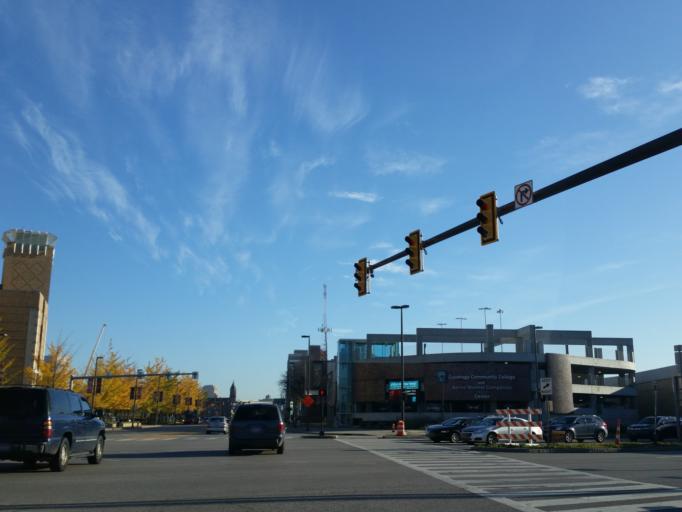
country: US
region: Ohio
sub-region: Cuyahoga County
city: Cleveland
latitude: 41.4942
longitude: -81.6855
